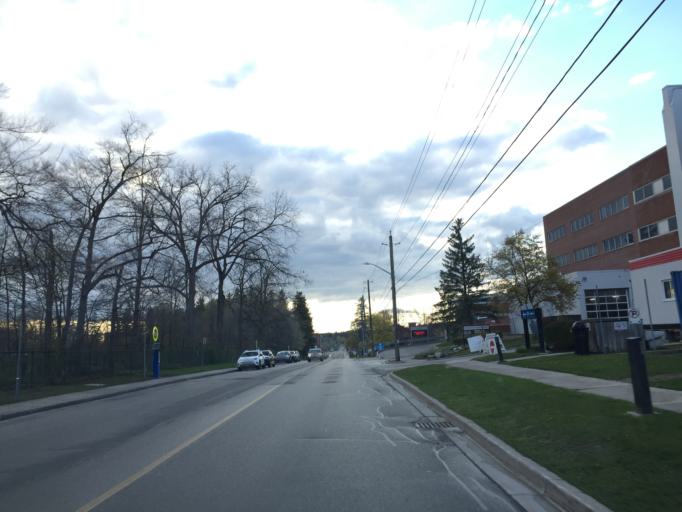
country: CA
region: Ontario
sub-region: Wellington County
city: Guelph
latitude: 43.5558
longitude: -80.2537
